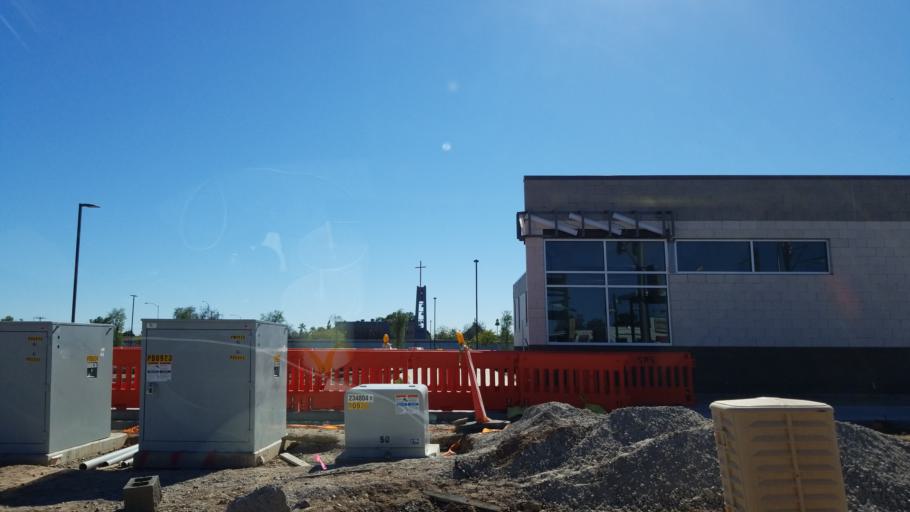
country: US
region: Arizona
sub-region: Maricopa County
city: Mesa
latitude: 33.4152
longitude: -111.7912
